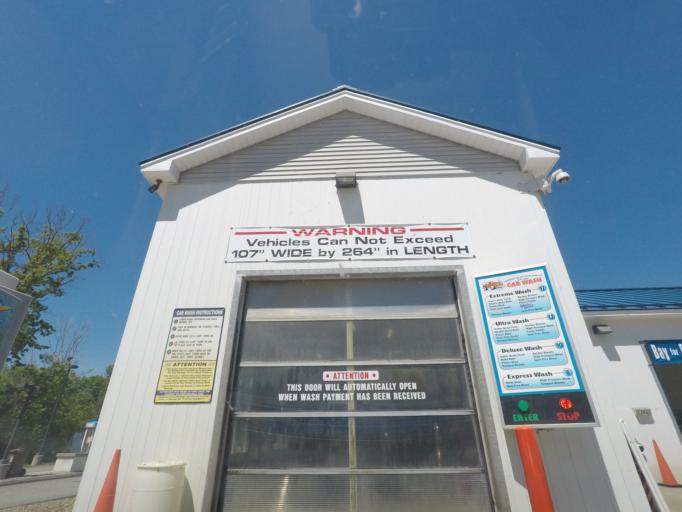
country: US
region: Maine
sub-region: Kennebec County
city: Gardiner
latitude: 44.2108
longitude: -69.7843
